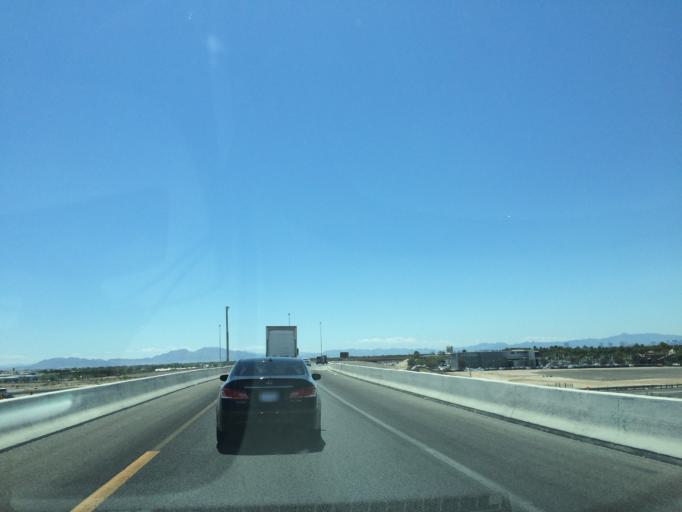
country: US
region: Nevada
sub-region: Clark County
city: Las Vegas
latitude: 36.2767
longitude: -115.2689
